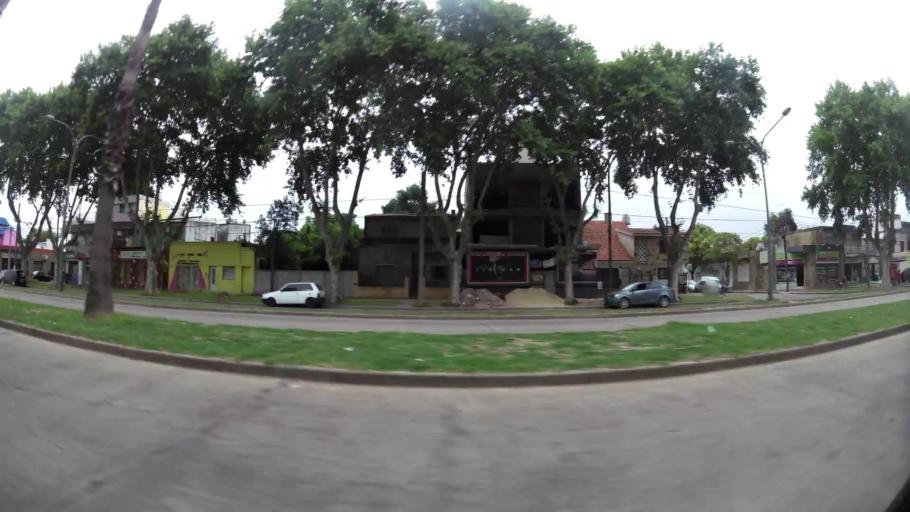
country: AR
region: Santa Fe
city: Granadero Baigorria
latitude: -32.8765
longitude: -60.6978
